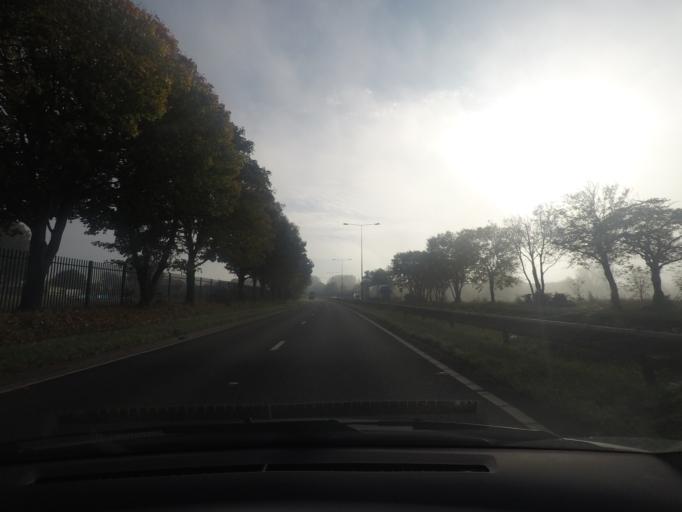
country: GB
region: England
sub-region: East Riding of Yorkshire
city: Welton
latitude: 53.7264
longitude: -0.5357
